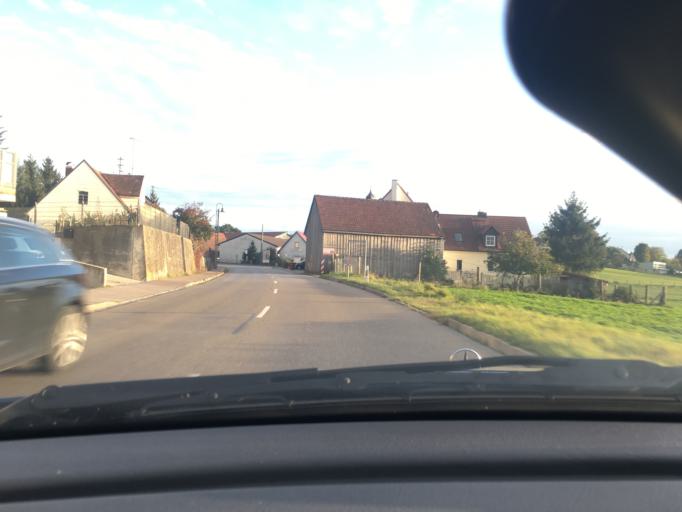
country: DE
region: Bavaria
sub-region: Swabia
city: Gablingen
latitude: 48.4141
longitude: 10.8242
